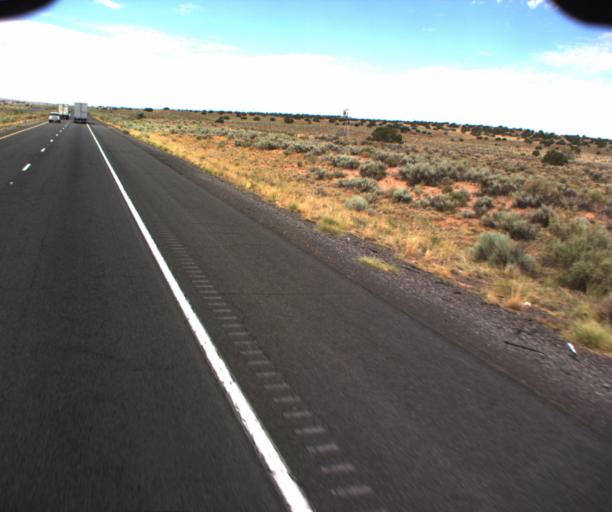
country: US
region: Arizona
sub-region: Apache County
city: Houck
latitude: 35.1545
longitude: -109.5018
